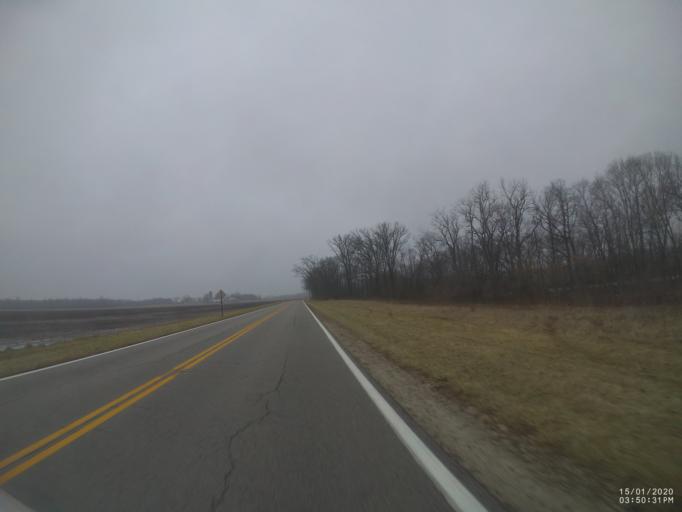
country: US
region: Ohio
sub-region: Wood County
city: Pemberville
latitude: 41.4245
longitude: -83.4126
